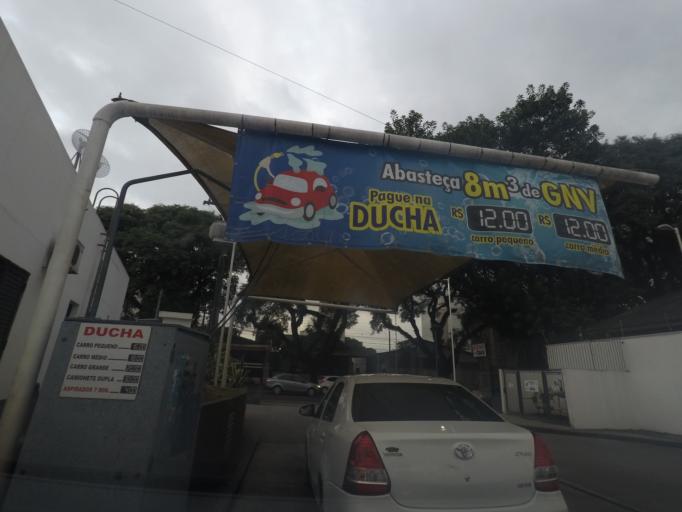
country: BR
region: Parana
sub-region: Curitiba
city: Curitiba
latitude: -25.4384
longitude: -49.2518
